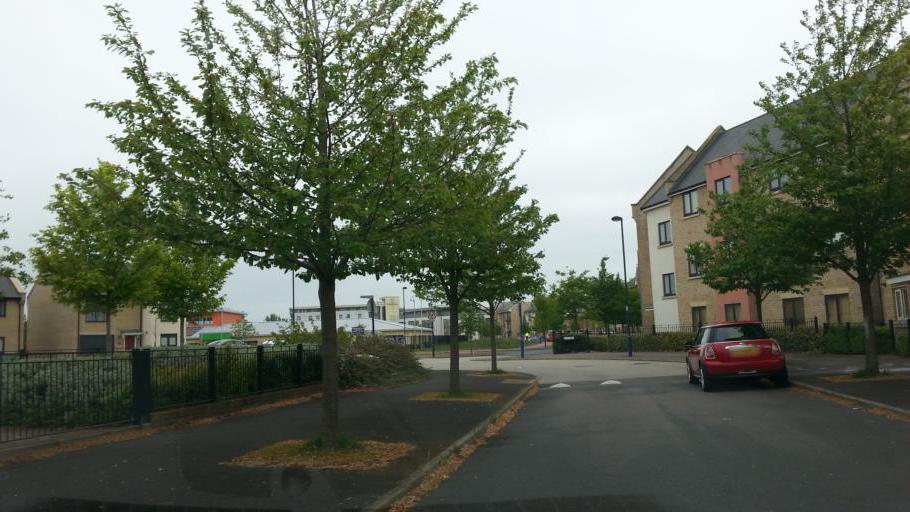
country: GB
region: England
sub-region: Cambridgeshire
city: Histon
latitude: 52.2323
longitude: 0.1160
